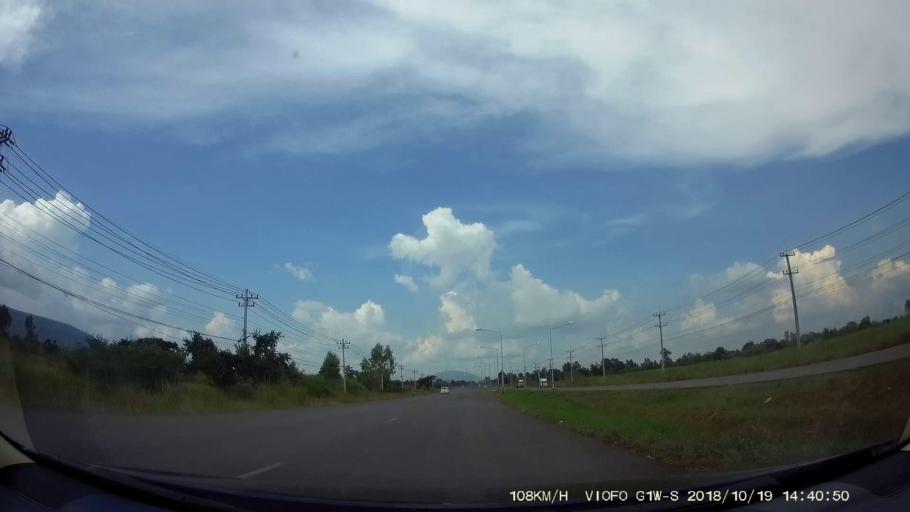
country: TH
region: Chaiyaphum
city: Phu Khiao
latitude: 16.2470
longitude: 102.1974
